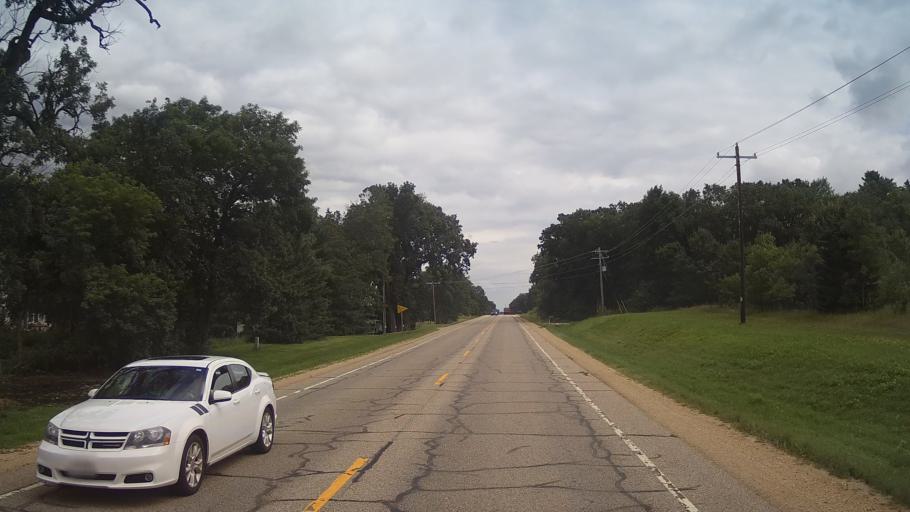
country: US
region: Wisconsin
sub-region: Waushara County
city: Wautoma
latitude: 44.0684
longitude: -89.3224
